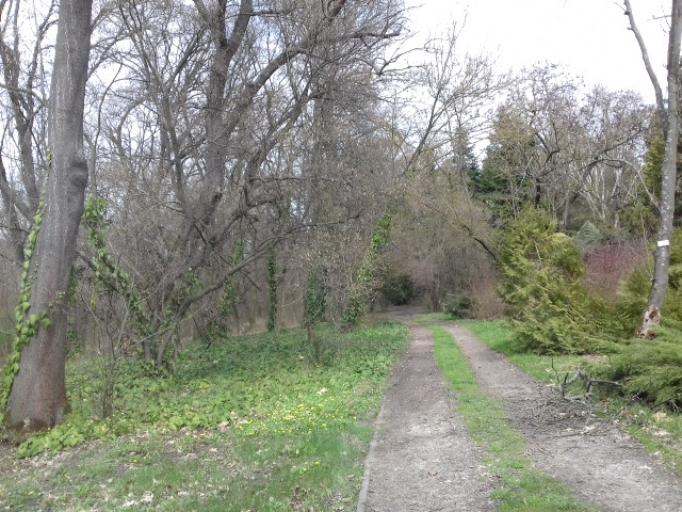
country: HU
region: Bacs-Kiskun
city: Tiszakecske
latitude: 46.8890
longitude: 20.1215
